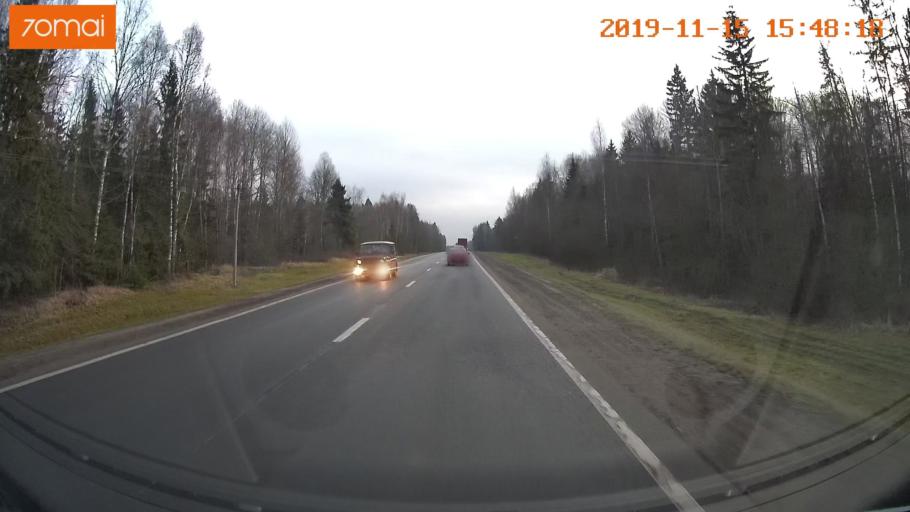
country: RU
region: Jaroslavl
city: Danilov
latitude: 57.9288
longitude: 40.0065
